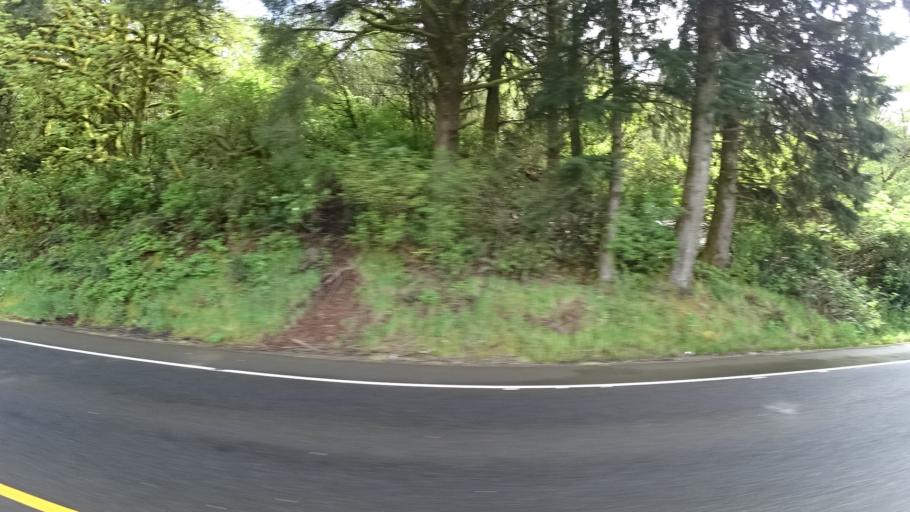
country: US
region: Oregon
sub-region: Lincoln County
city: Rose Lodge
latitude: 45.0199
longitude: -123.9459
